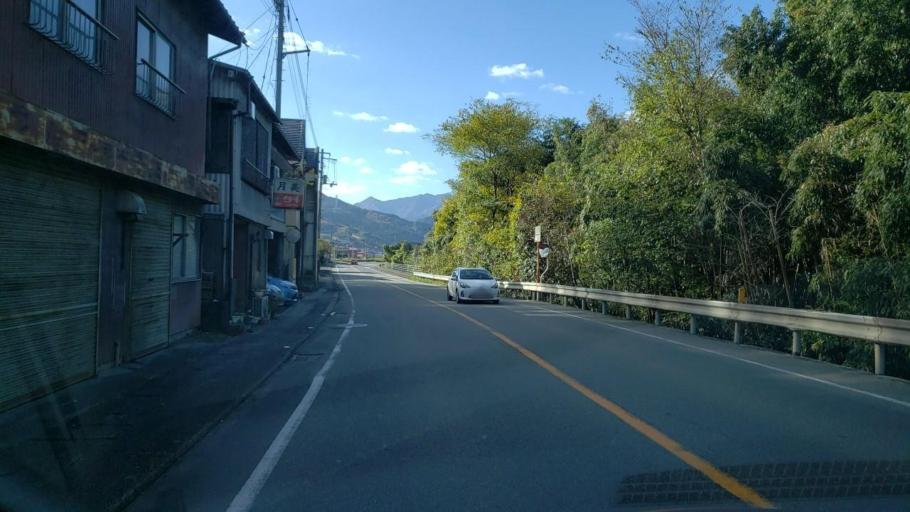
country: JP
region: Tokushima
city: Wakimachi
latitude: 34.0552
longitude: 134.1787
